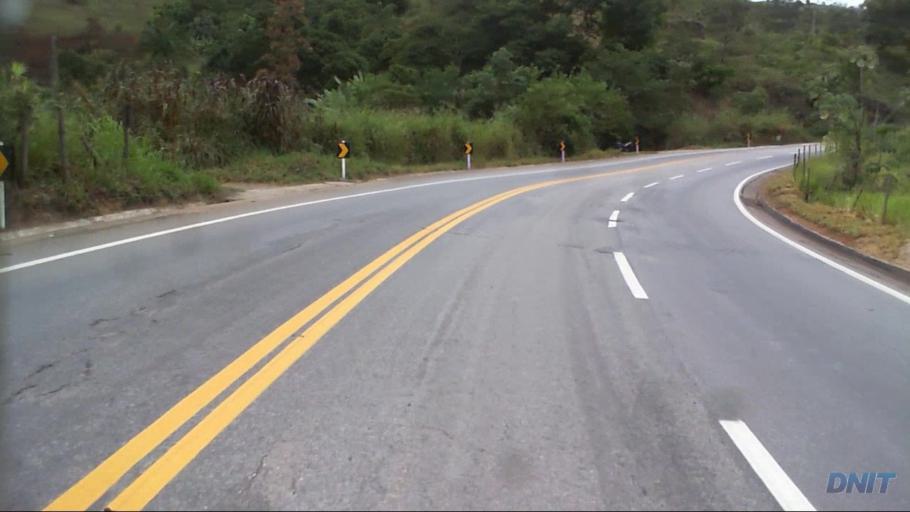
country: BR
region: Minas Gerais
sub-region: Timoteo
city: Timoteo
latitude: -19.6371
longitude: -42.8294
